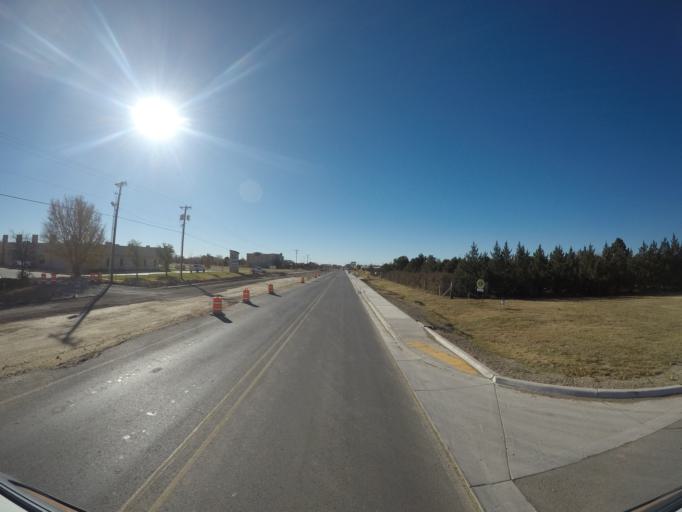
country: US
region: New Mexico
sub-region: Curry County
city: Clovis
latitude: 34.4437
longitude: -103.1965
